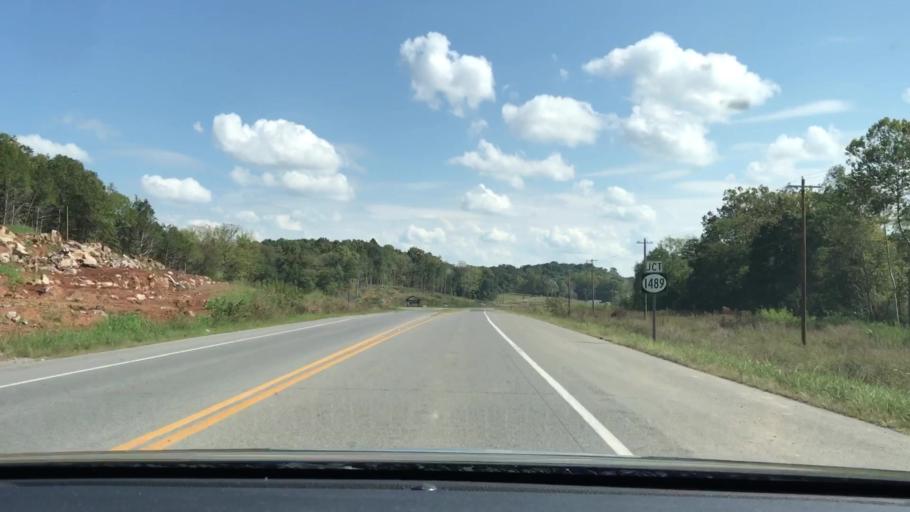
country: US
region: Kentucky
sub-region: Trigg County
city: Cadiz
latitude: 36.8047
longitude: -87.9313
